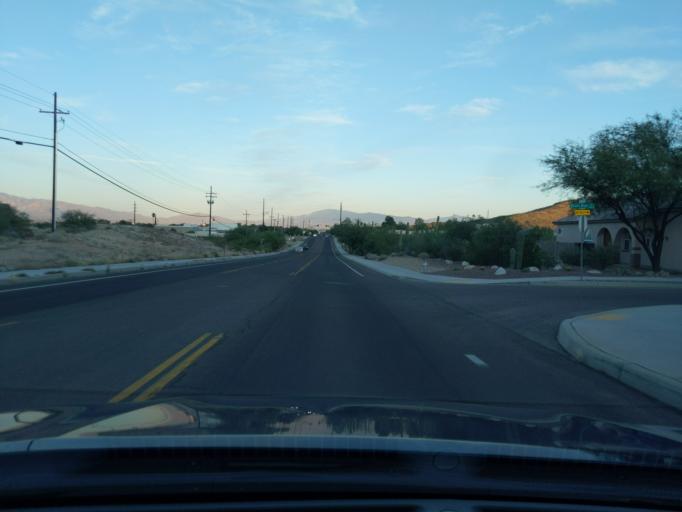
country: US
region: Arizona
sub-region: Pima County
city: South Tucson
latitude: 32.2249
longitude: -111.0322
